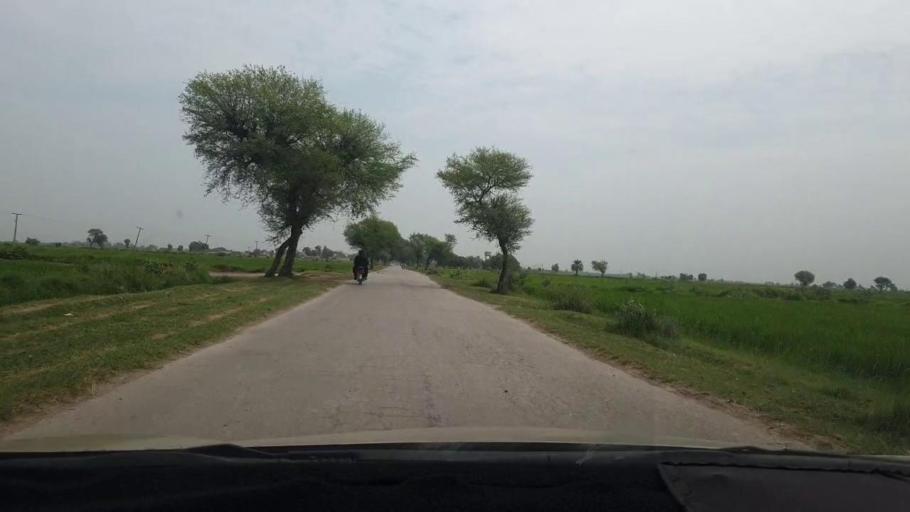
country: PK
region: Sindh
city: Ratodero
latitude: 27.7538
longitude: 68.3224
